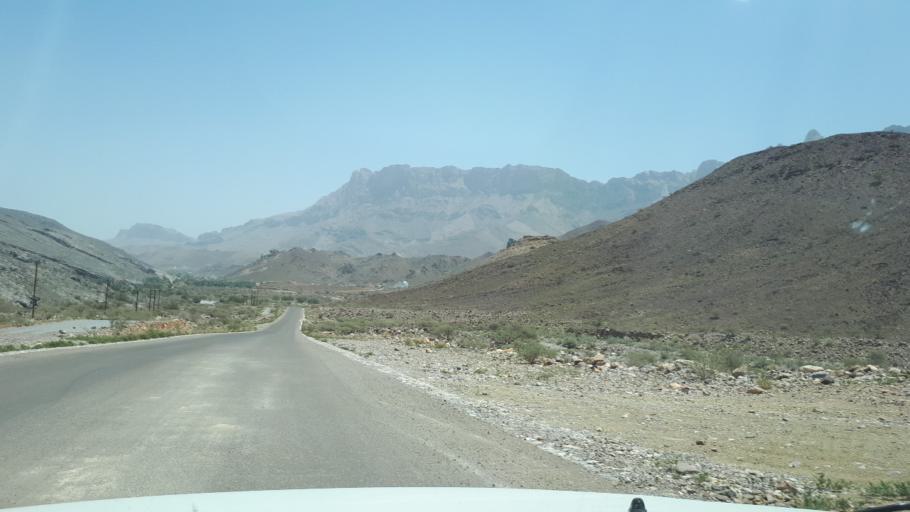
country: OM
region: Muhafazat ad Dakhiliyah
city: Bahla'
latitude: 23.1820
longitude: 57.1406
